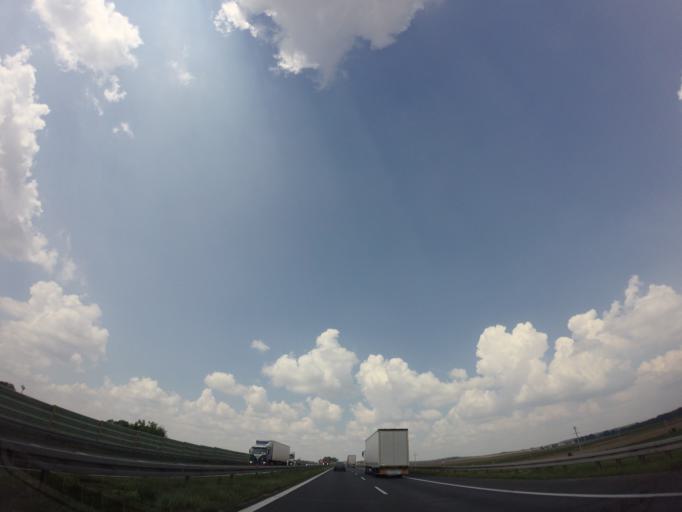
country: PL
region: Silesian Voivodeship
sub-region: Powiat gliwicki
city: Rudziniec
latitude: 50.4128
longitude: 18.4082
